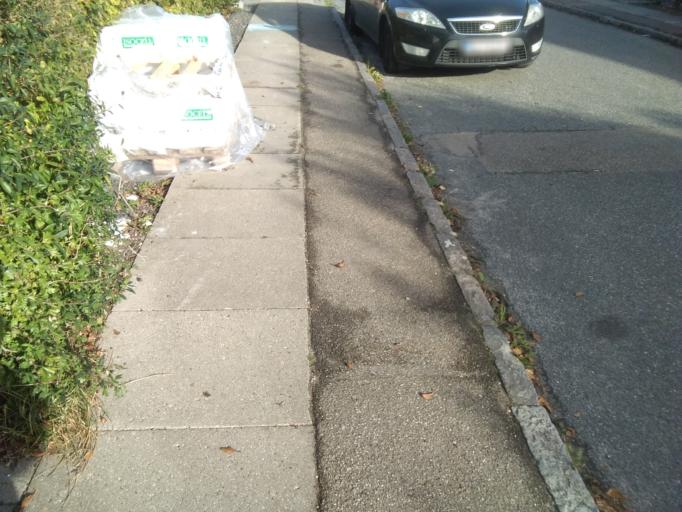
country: DK
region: Capital Region
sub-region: Kobenhavn
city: Vanlose
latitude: 55.6985
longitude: 12.4939
